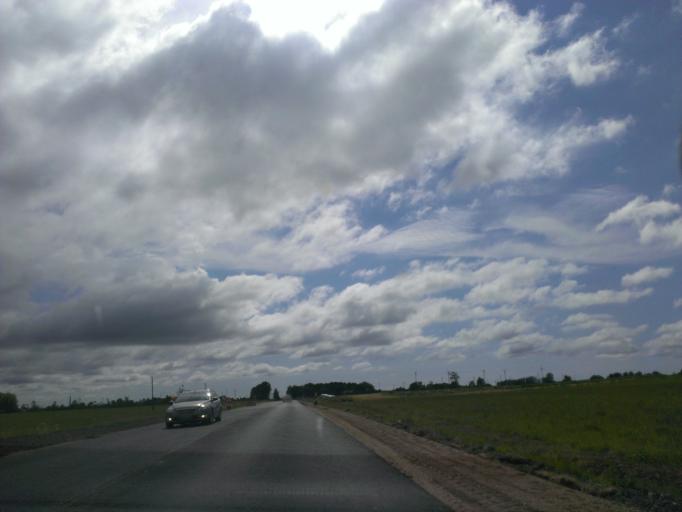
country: LV
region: Durbe
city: Liegi
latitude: 56.5706
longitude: 21.2813
